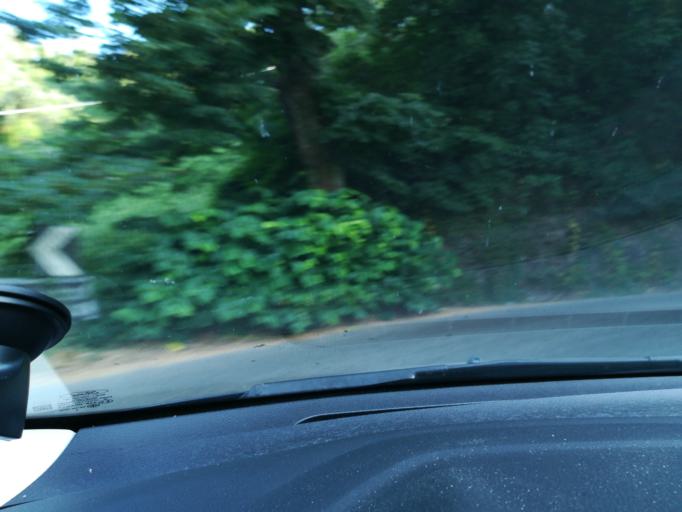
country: IT
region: Tuscany
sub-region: Provincia di Lucca
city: Stiava
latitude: 43.9137
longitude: 10.3413
